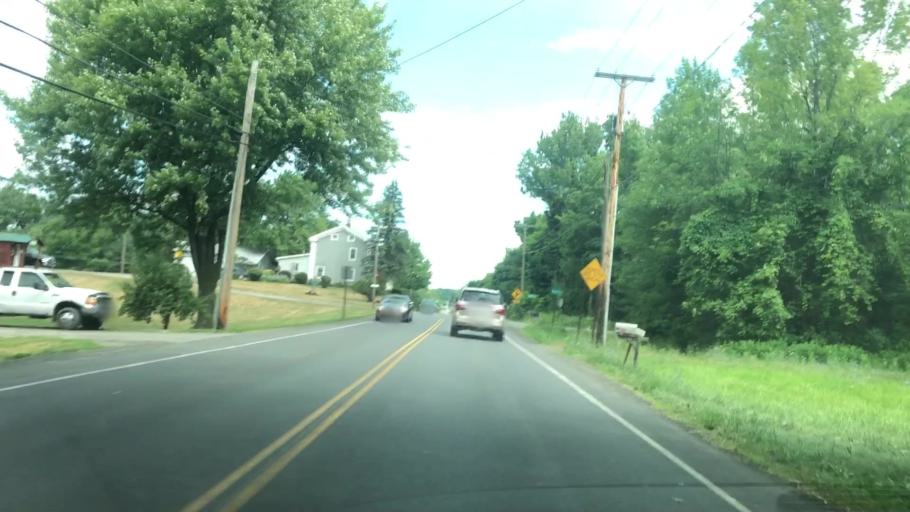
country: US
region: New York
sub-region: Wayne County
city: Macedon
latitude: 43.0713
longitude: -77.3612
